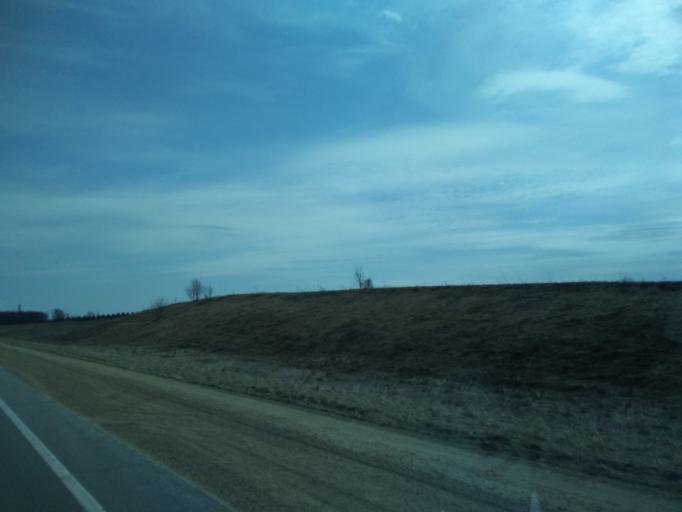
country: US
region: Iowa
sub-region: Winneshiek County
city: Decorah
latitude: 43.3756
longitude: -91.8149
